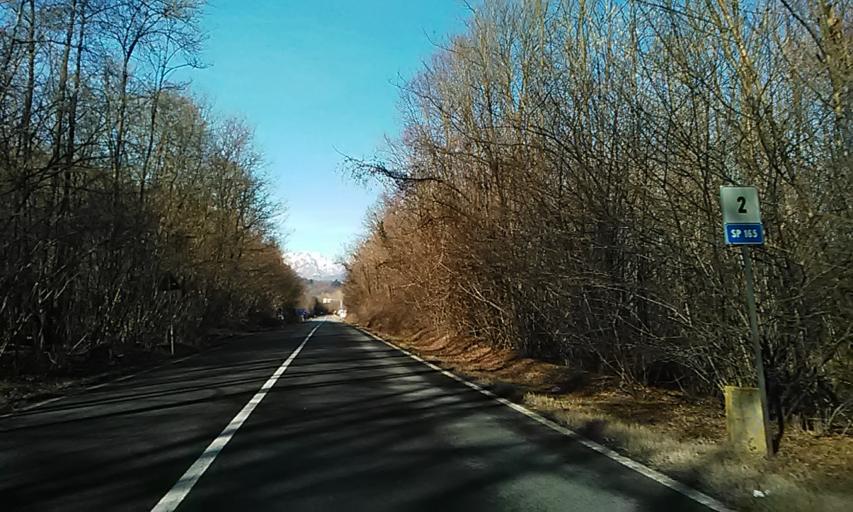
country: IT
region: Piedmont
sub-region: Provincia di Novara
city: Prato Sesia
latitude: 45.6490
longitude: 8.3563
